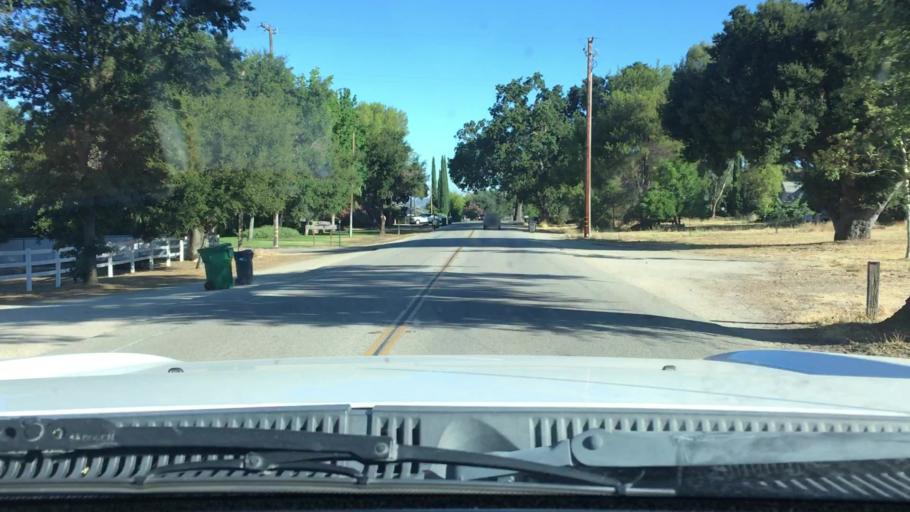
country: US
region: California
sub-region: San Luis Obispo County
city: Templeton
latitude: 35.5179
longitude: -120.7011
